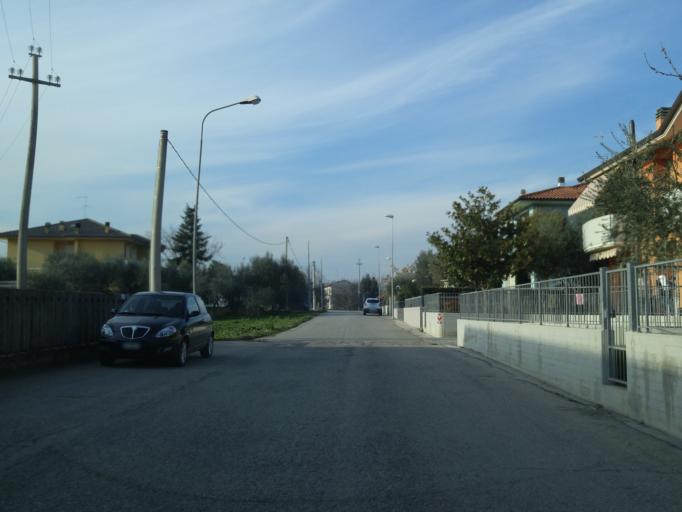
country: IT
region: The Marches
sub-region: Provincia di Pesaro e Urbino
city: Lucrezia
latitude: 43.7679
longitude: 12.9478
